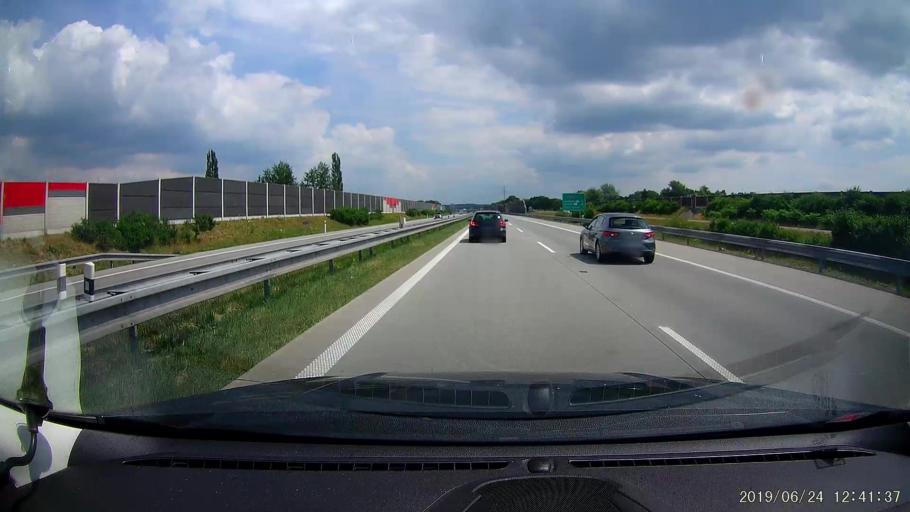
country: CZ
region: Moravskoslezsky
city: Bohumin
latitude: 49.9181
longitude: 18.3665
